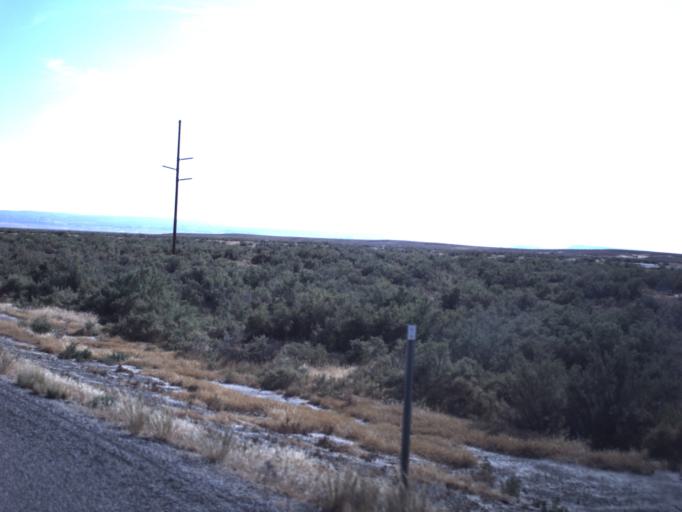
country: US
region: Utah
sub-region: Grand County
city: Moab
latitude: 38.8789
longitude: -109.8129
